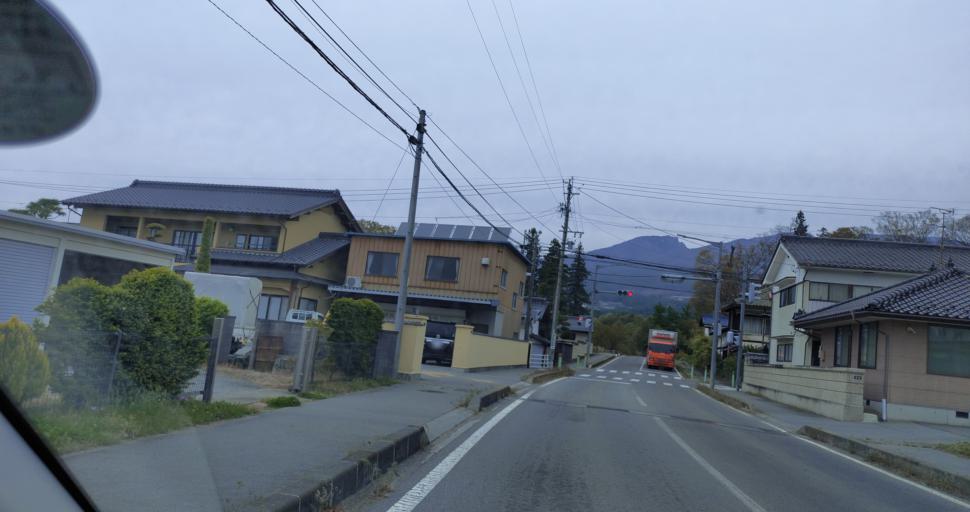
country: JP
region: Nagano
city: Komoro
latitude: 36.3212
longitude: 138.4928
